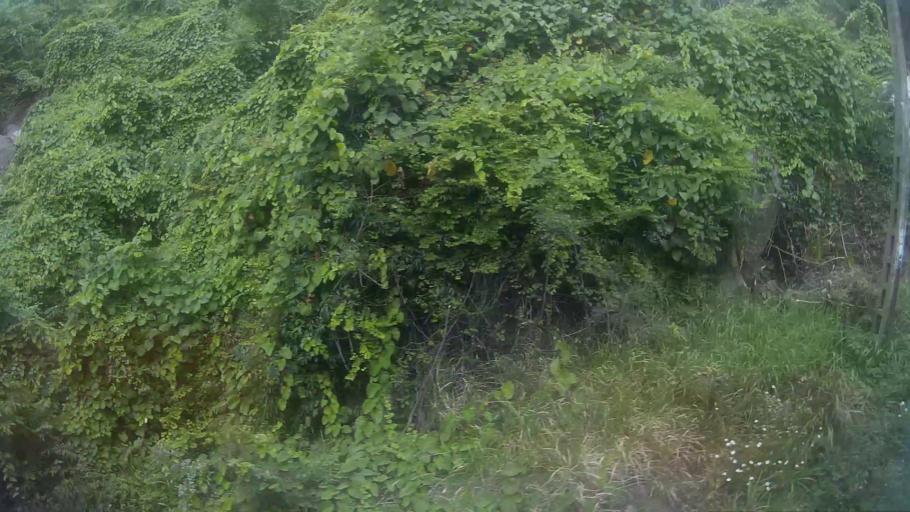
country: VN
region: Khanh Hoa
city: Van Gia
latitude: 12.8500
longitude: 109.3914
